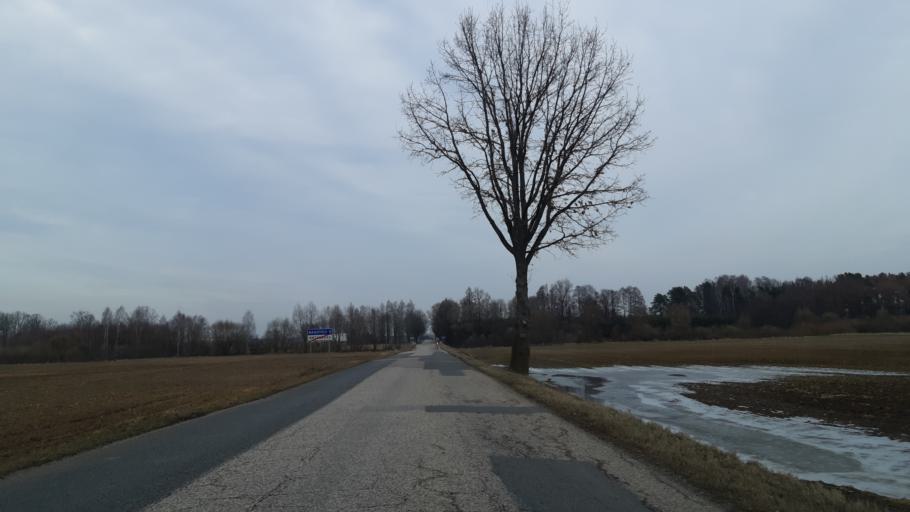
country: LT
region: Marijampoles apskritis
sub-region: Marijampole Municipality
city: Marijampole
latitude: 54.7114
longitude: 23.3165
